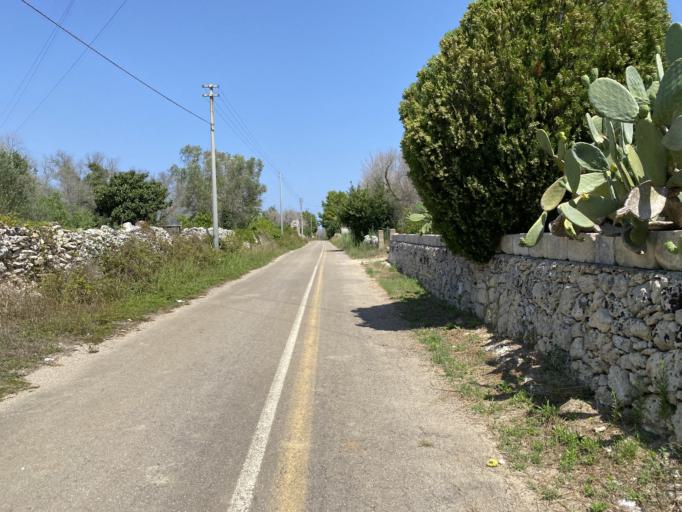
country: IT
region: Apulia
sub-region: Provincia di Lecce
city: Sanarica
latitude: 40.0955
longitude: 18.3536
